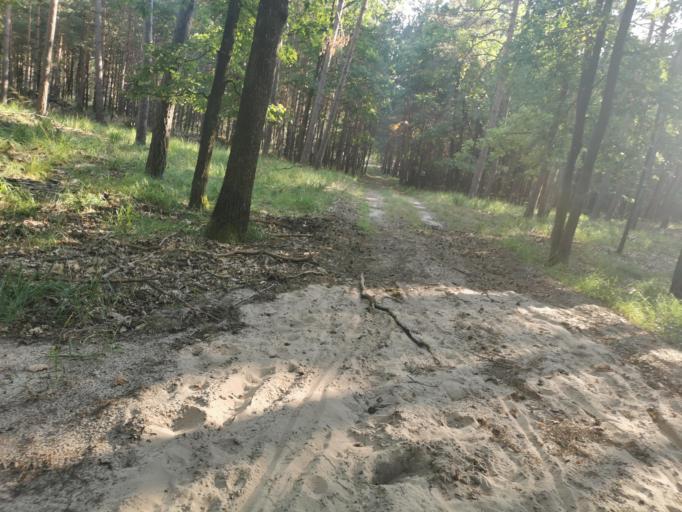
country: SK
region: Trnavsky
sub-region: Okres Senica
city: Senica
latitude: 48.6378
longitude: 17.2945
